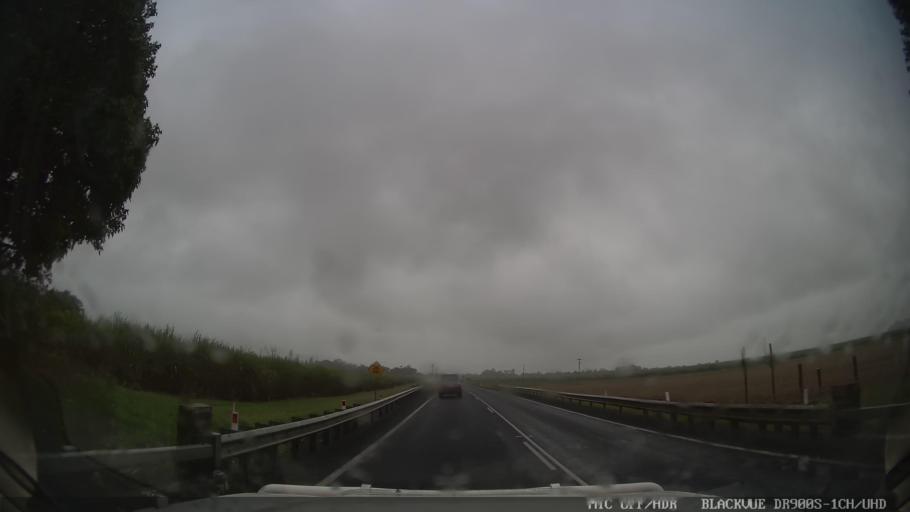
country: AU
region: Queensland
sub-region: Cassowary Coast
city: Innisfail
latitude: -17.6492
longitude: 146.0326
